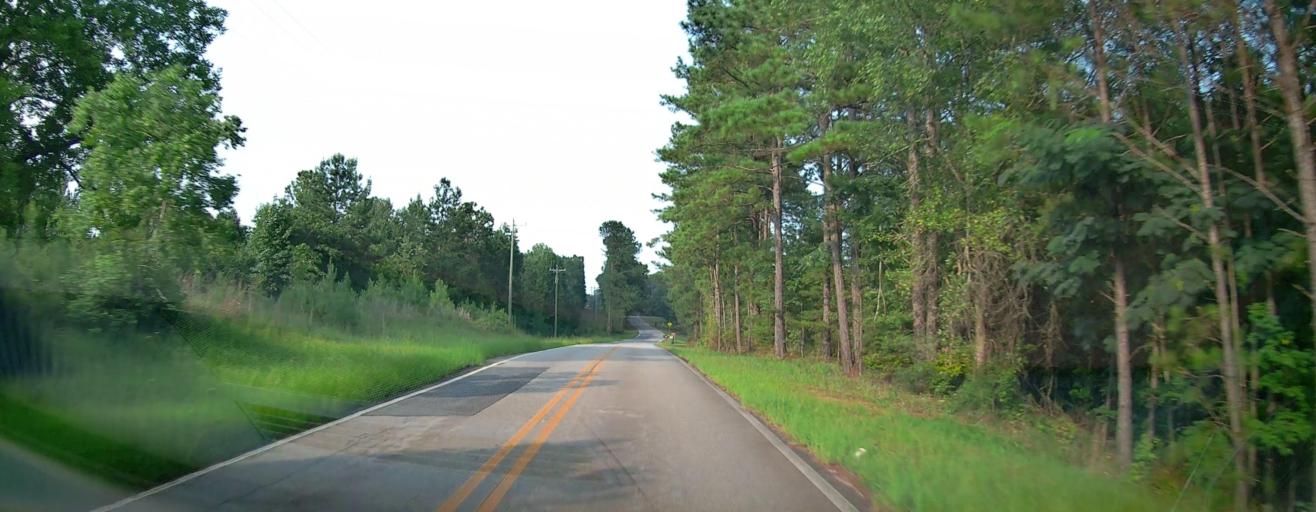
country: US
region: Georgia
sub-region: Monroe County
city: Forsyth
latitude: 32.9711
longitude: -83.8074
